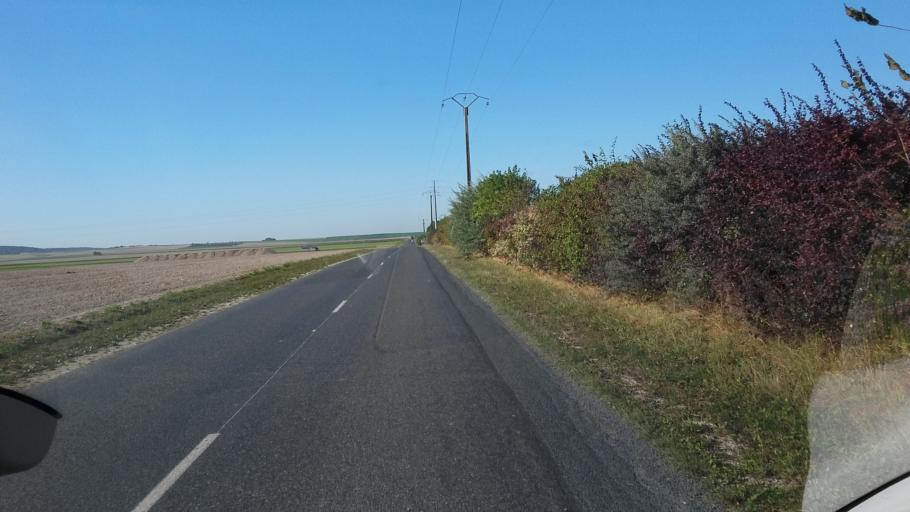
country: FR
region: Champagne-Ardenne
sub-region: Departement de la Marne
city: Connantre
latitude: 48.7372
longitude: 3.9002
